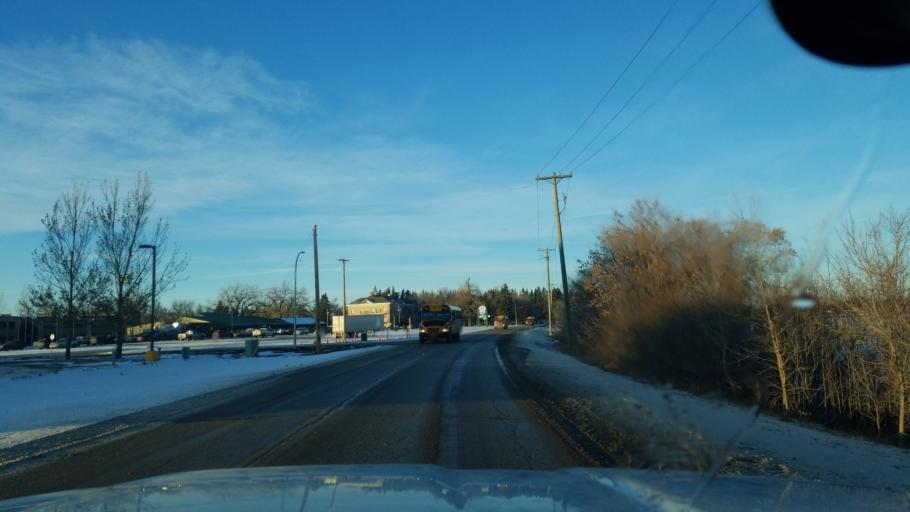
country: CA
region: Manitoba
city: Portage la Prairie
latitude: 49.9594
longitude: -98.3213
